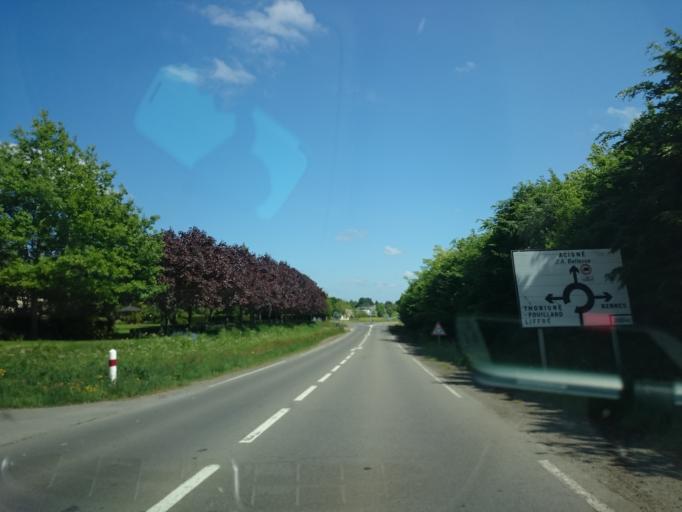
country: FR
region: Brittany
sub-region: Departement d'Ille-et-Vilaine
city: Fouillard
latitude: 48.1551
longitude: -1.5970
